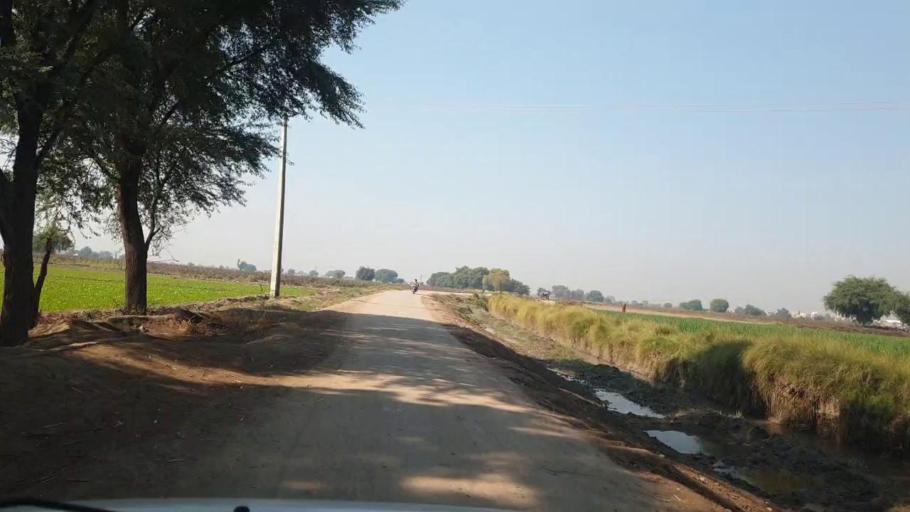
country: PK
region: Sindh
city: Bhan
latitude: 26.6420
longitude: 67.7137
